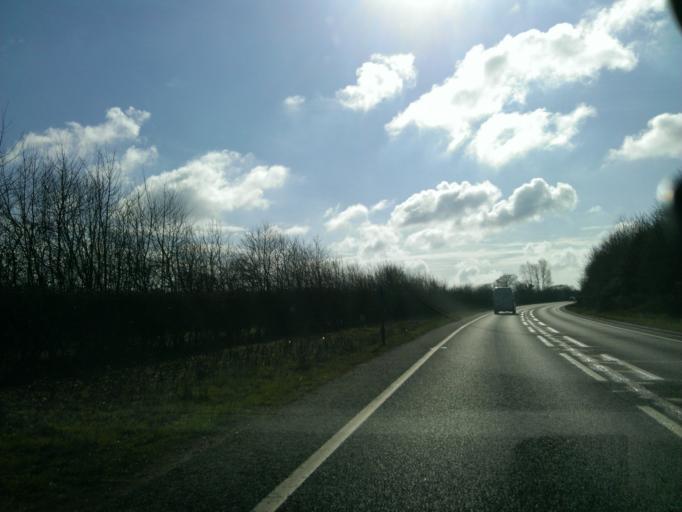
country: GB
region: England
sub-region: Essex
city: Little Clacton
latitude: 51.8382
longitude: 1.1221
